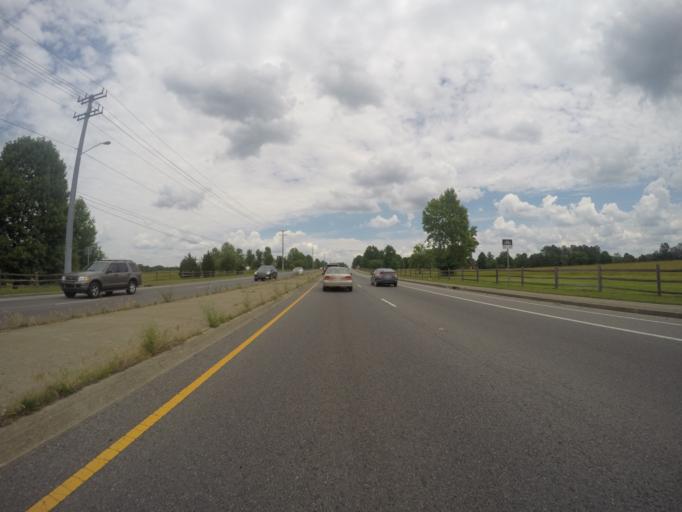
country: US
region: Tennessee
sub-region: Davidson County
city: Lakewood
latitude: 36.2100
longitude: -86.6095
